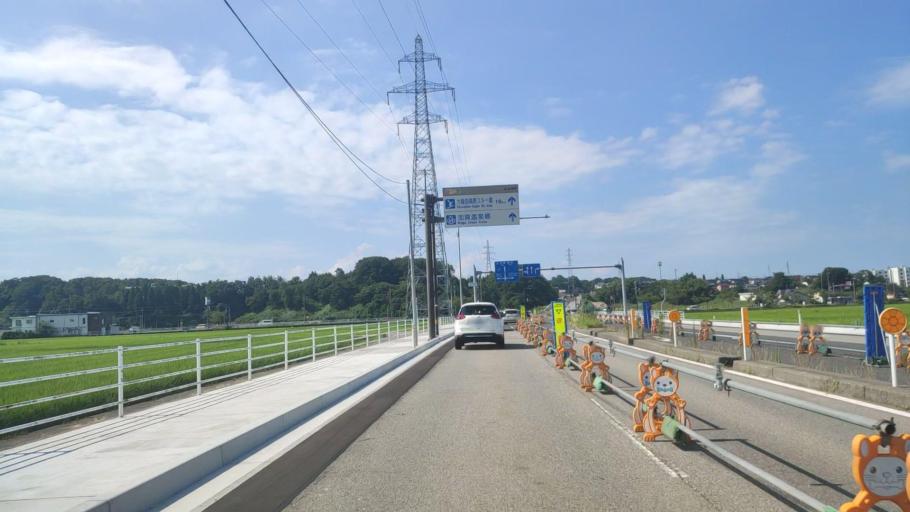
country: JP
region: Ishikawa
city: Komatsu
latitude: 36.4025
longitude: 136.5073
